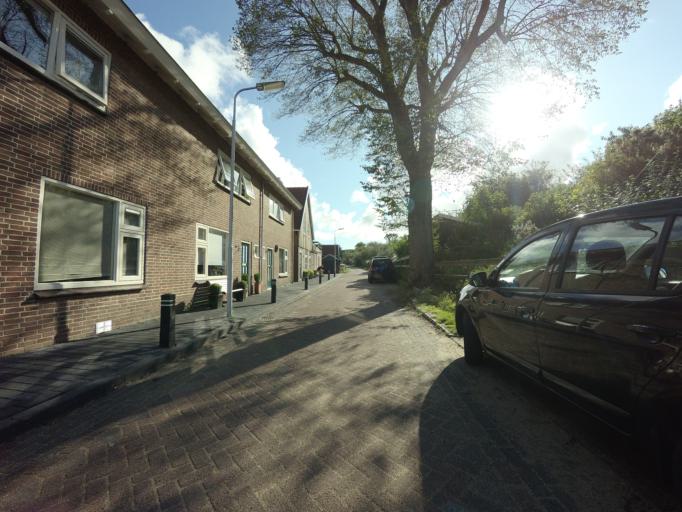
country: NL
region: Friesland
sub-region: Gemeente Terschelling
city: West-Terschelling
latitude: 53.3614
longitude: 5.2135
